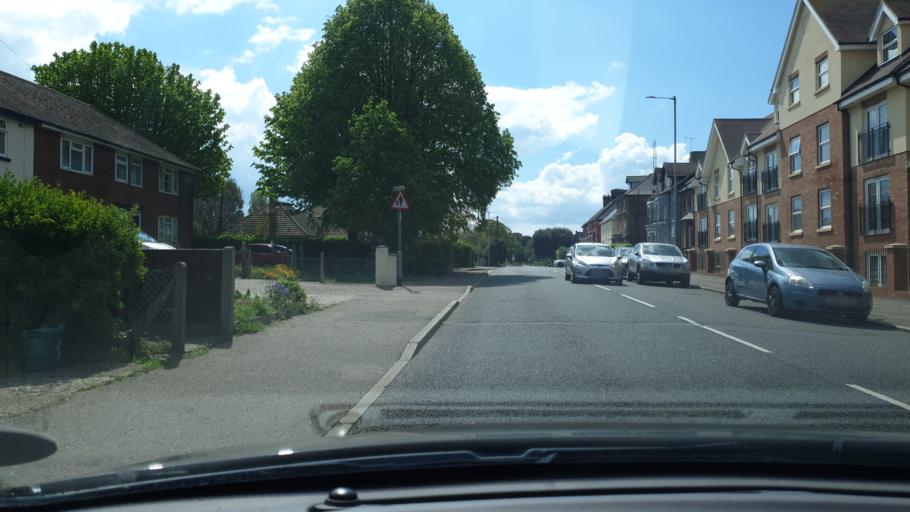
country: GB
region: England
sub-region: Essex
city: Harwich
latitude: 51.9417
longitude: 1.2870
